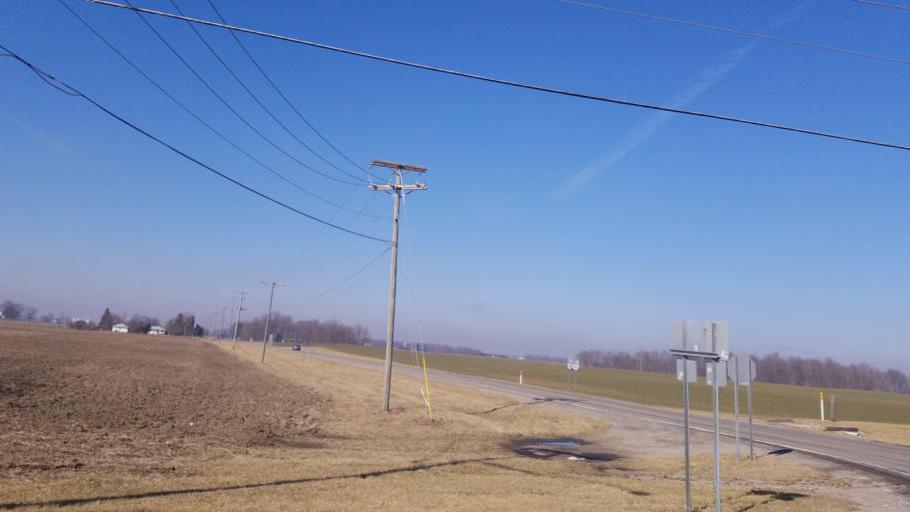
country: US
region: Ohio
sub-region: Crawford County
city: Bucyrus
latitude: 40.8339
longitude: -82.9714
